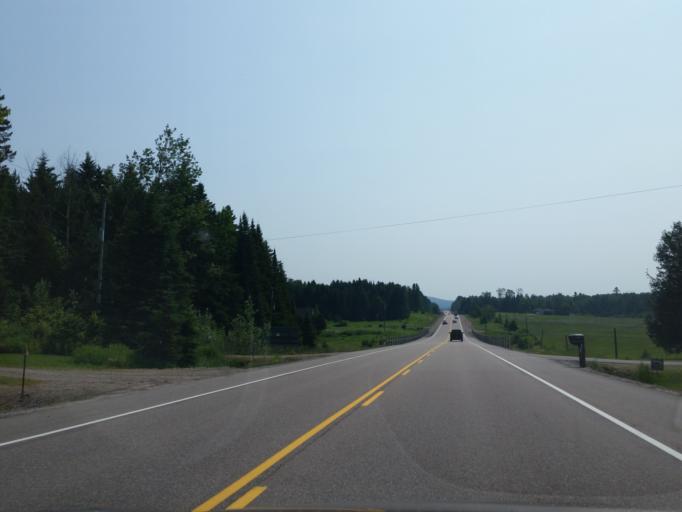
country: CA
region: Ontario
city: Mattawa
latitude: 46.3062
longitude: -78.6232
